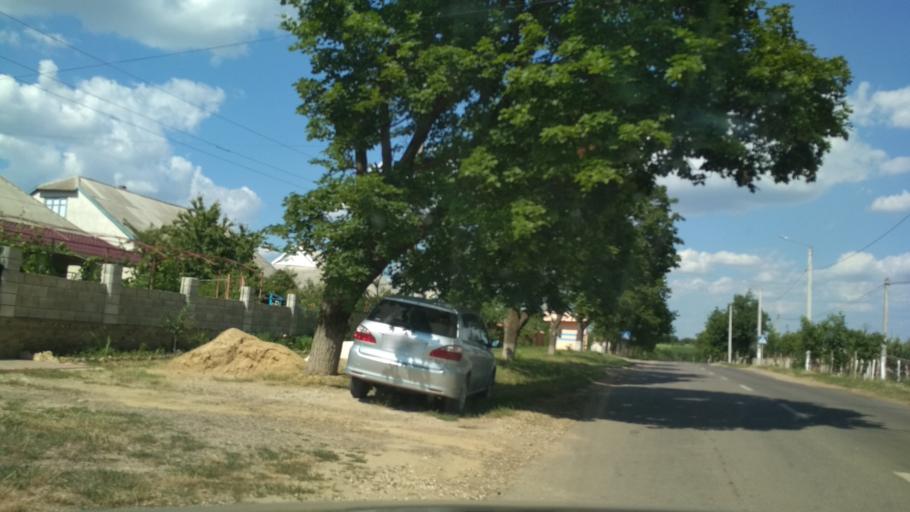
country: MD
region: Criuleni
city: Criuleni
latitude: 47.1770
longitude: 29.2009
